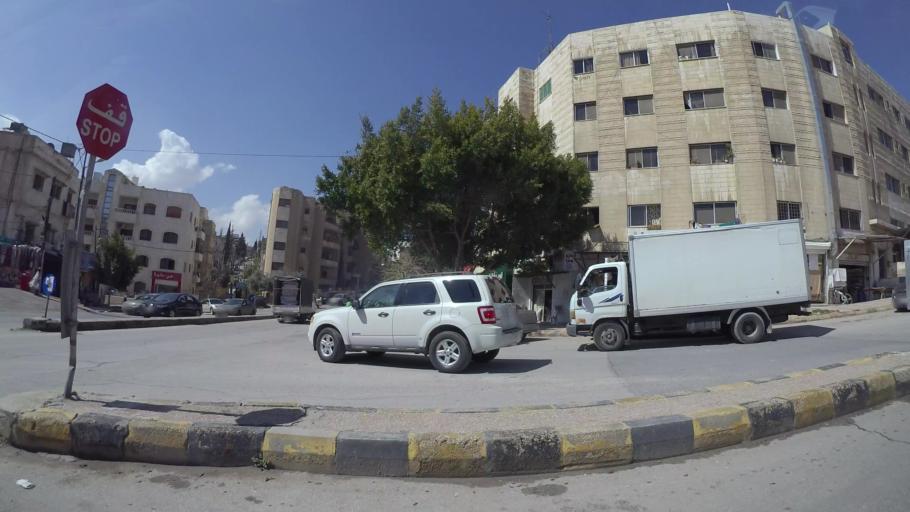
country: JO
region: Amman
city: Amman
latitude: 31.9807
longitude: 35.9945
